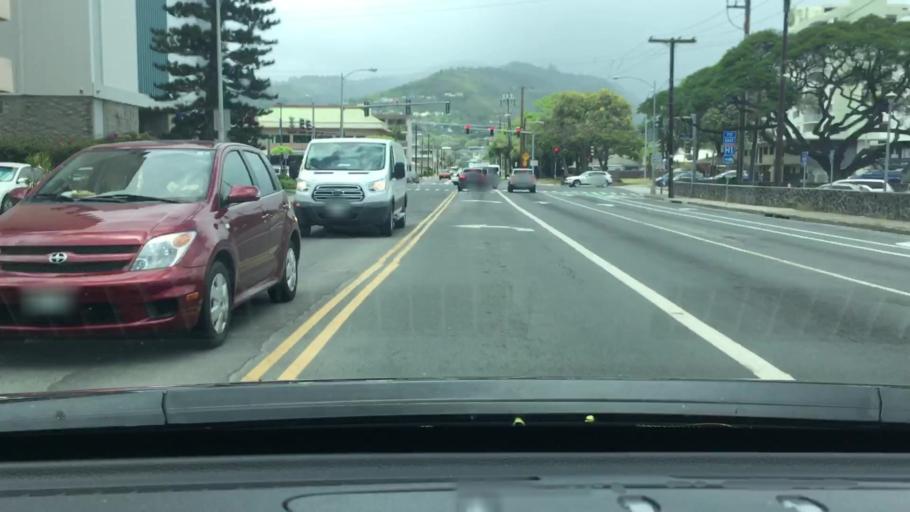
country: US
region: Hawaii
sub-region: Honolulu County
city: Honolulu
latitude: 21.2888
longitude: -157.8327
